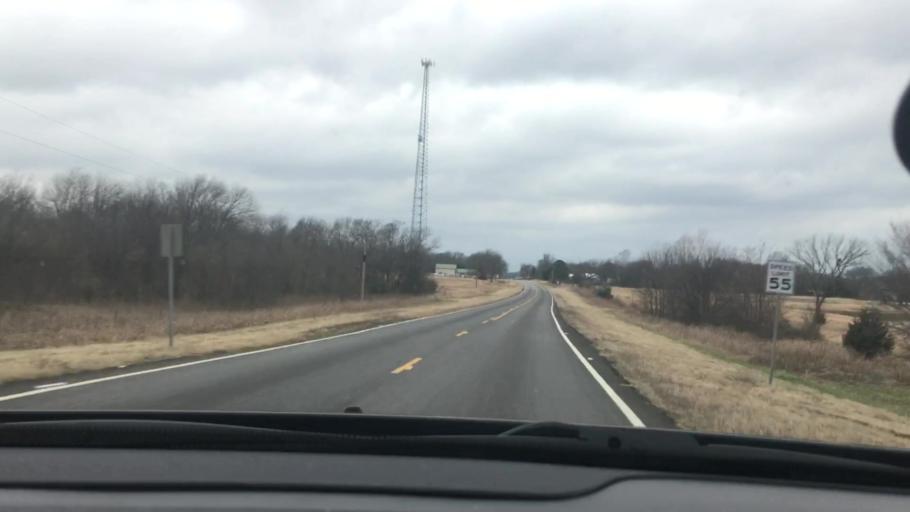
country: US
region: Oklahoma
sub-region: Coal County
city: Coalgate
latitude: 34.3749
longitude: -96.4116
